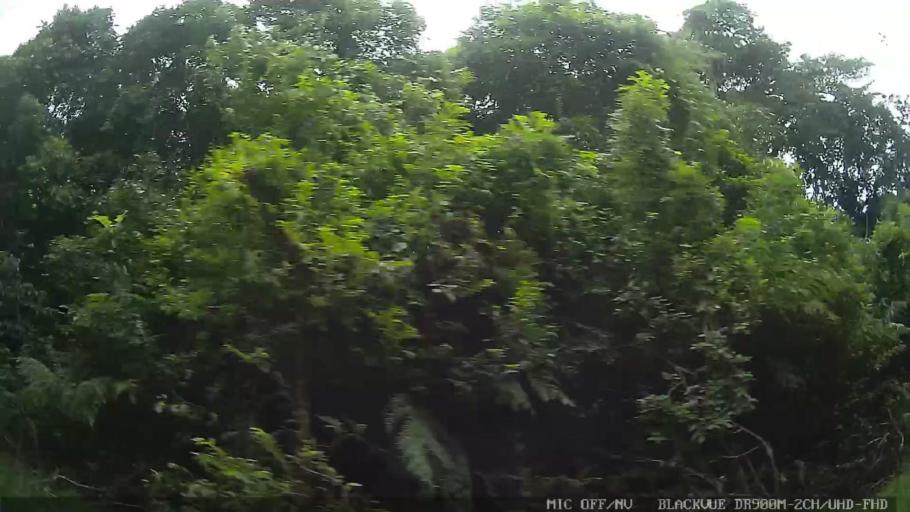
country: BR
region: Sao Paulo
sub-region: Iguape
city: Iguape
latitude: -24.6863
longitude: -47.4849
